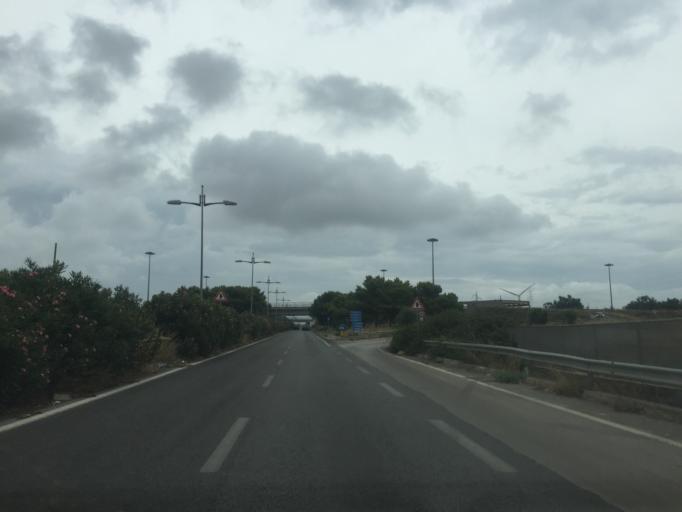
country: IT
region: Sicily
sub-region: Ragusa
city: Ragusa
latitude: 36.8913
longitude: 14.6958
